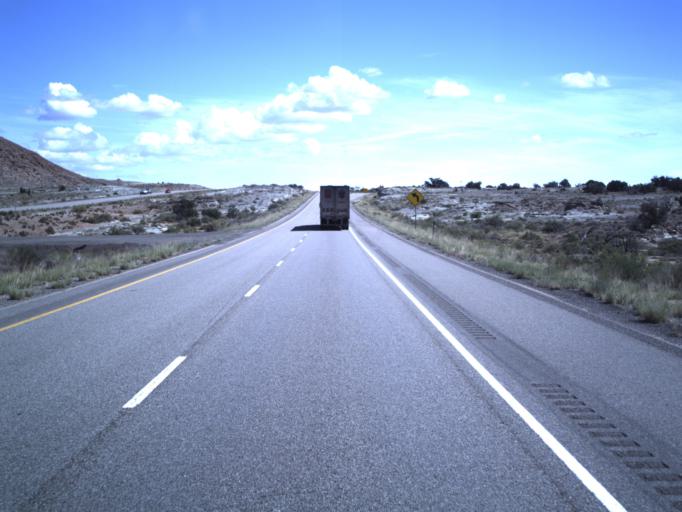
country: US
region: Utah
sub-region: Emery County
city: Ferron
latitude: 38.8310
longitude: -111.1268
